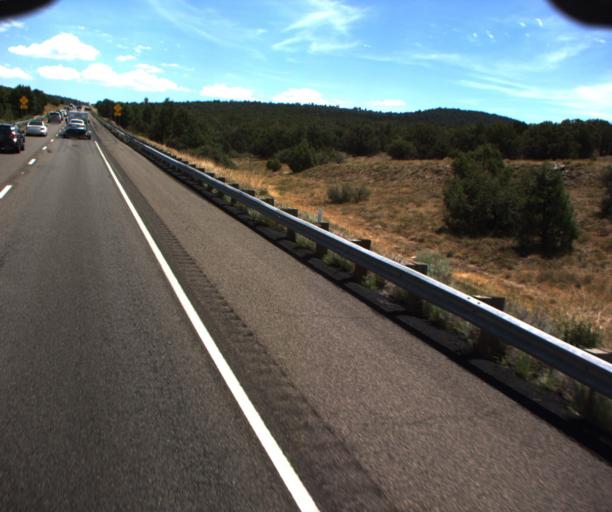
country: US
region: Arizona
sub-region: Yavapai County
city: Village of Oak Creek (Big Park)
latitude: 34.7826
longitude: -111.6115
